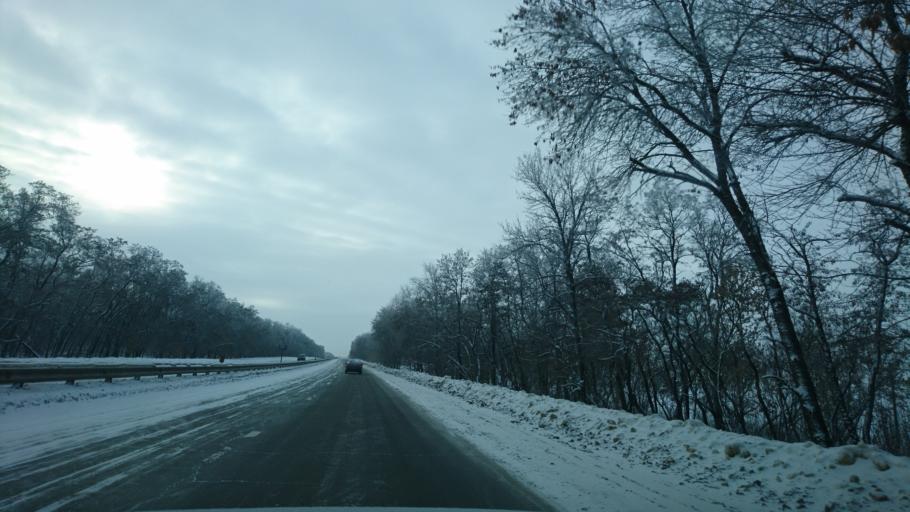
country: RU
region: Belgorod
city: Mayskiy
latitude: 50.4811
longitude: 36.4063
